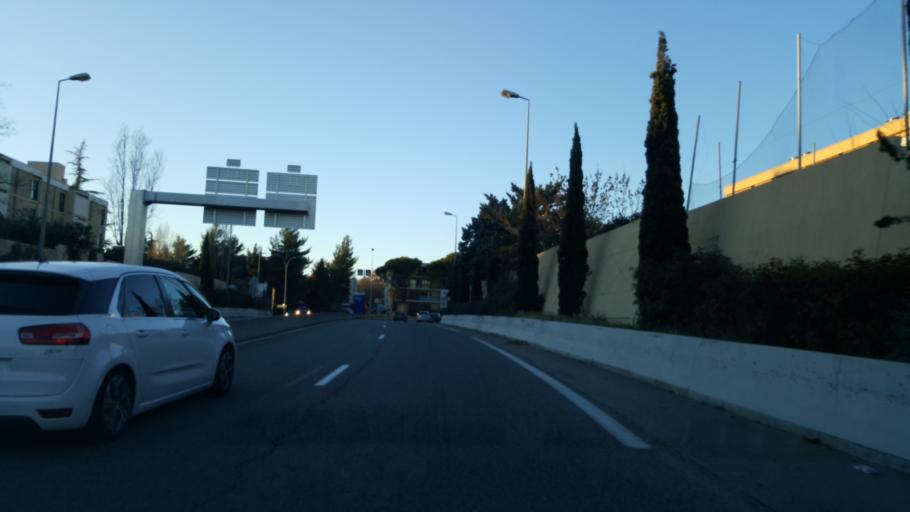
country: FR
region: Provence-Alpes-Cote d'Azur
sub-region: Departement des Bouches-du-Rhone
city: Aix-en-Provence
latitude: 43.5144
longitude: 5.4673
